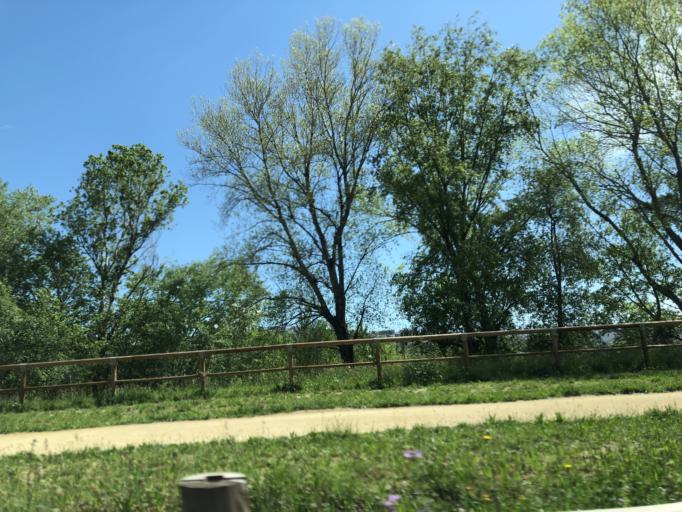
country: FR
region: Provence-Alpes-Cote d'Azur
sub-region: Departement des Alpes-Maritimes
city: Saint-Laurent-du-Var
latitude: 43.6796
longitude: 7.1905
